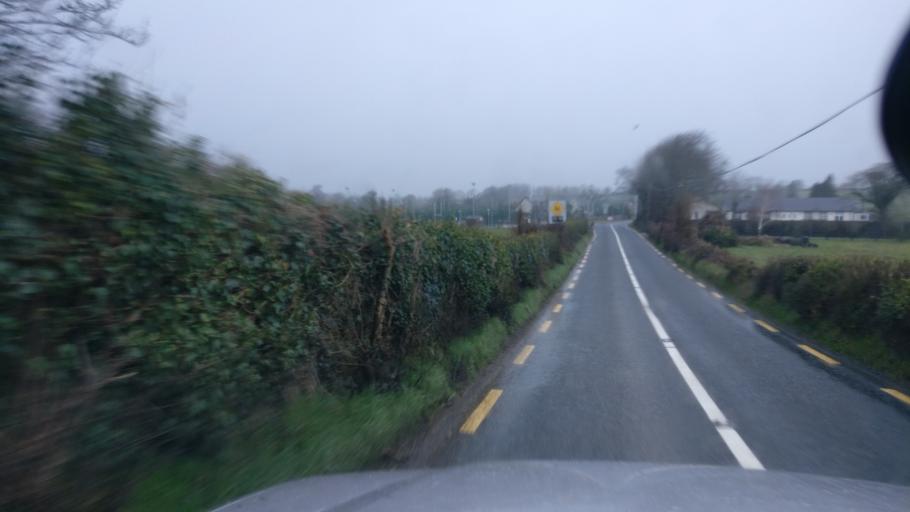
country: IE
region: Connaught
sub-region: County Galway
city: Loughrea
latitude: 53.1584
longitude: -8.4844
